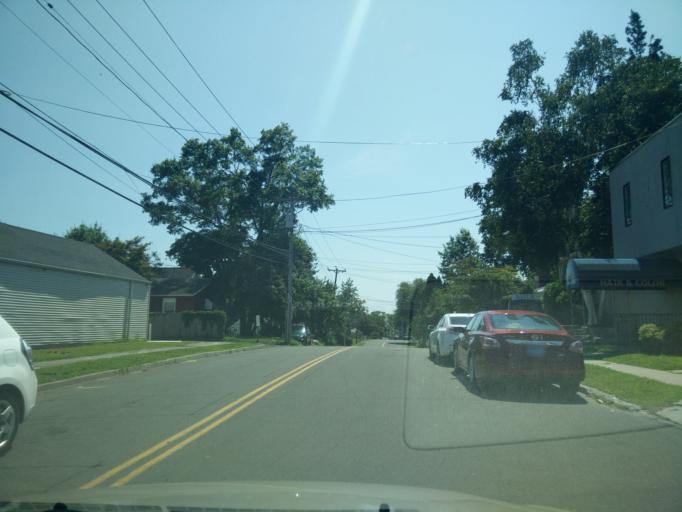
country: US
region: Connecticut
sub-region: Fairfield County
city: Bridgeport
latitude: 41.1767
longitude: -73.2328
